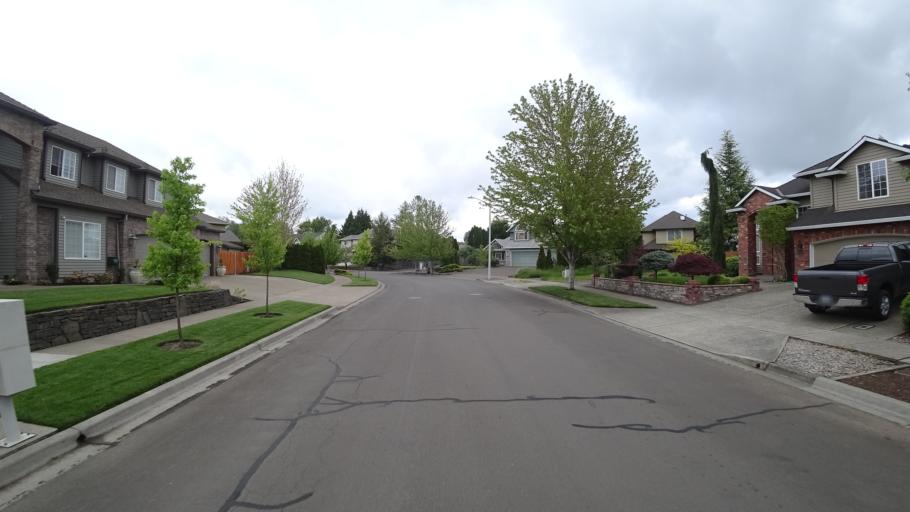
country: US
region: Oregon
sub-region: Washington County
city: Hillsboro
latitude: 45.5472
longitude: -122.9867
